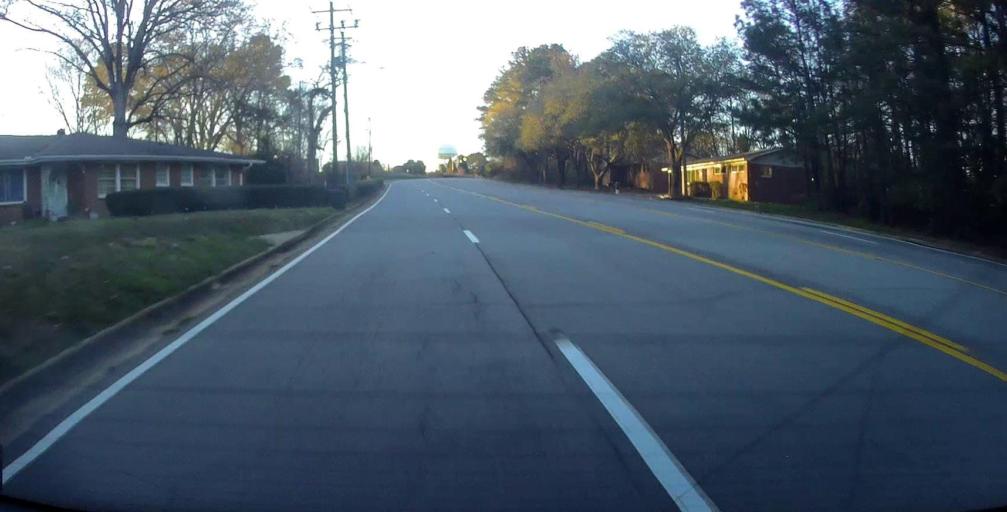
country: US
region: Alabama
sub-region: Russell County
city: Phenix City
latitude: 32.5156
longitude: -84.9854
